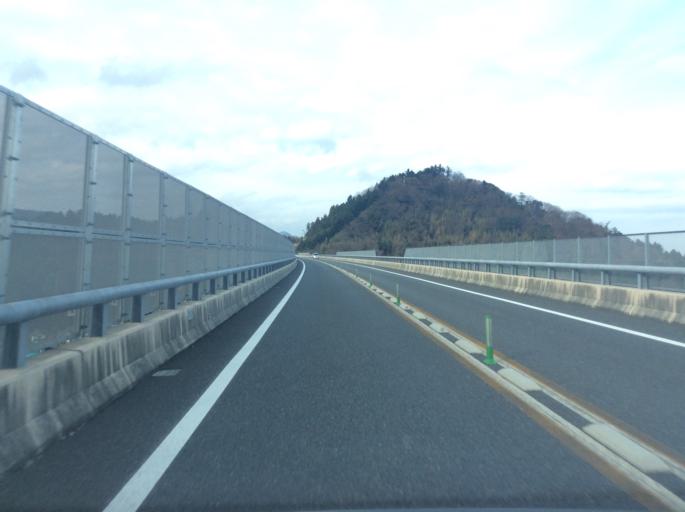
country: JP
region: Fukushima
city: Iwaki
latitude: 37.2013
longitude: 140.9858
